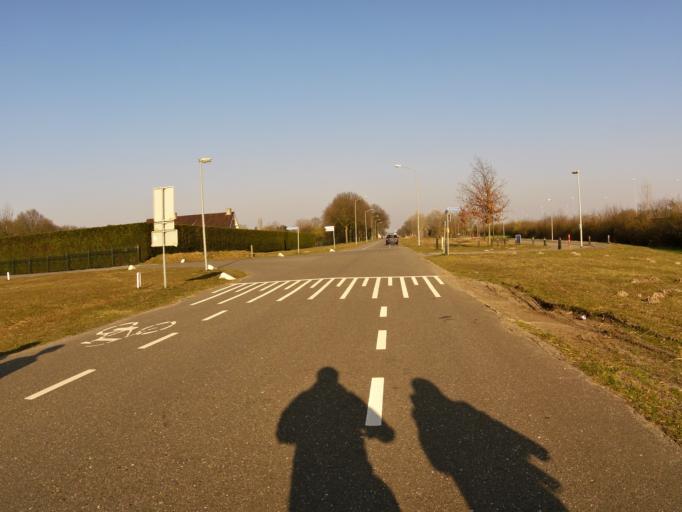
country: NL
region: North Brabant
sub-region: Gemeente Maasdonk
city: Geffen
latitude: 51.7180
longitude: 5.4308
